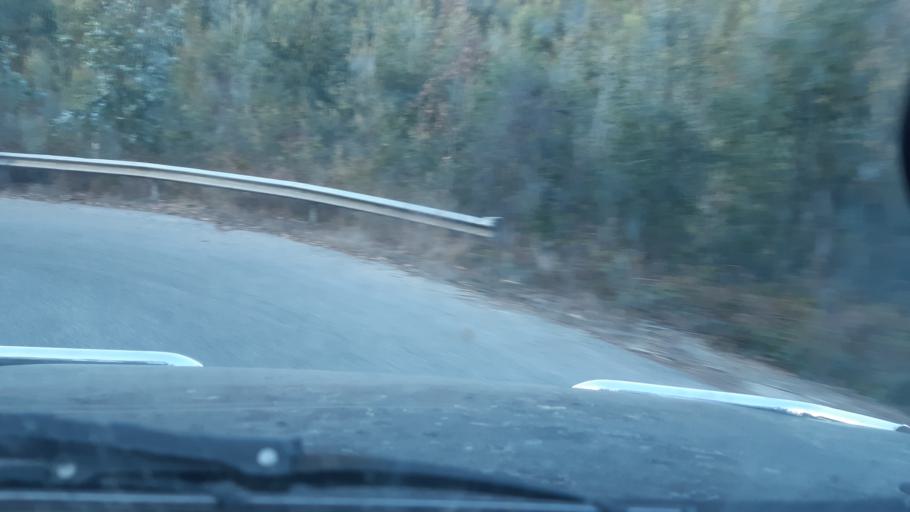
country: PT
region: Aveiro
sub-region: Agueda
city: Aguada de Cima
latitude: 40.5675
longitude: -8.3538
